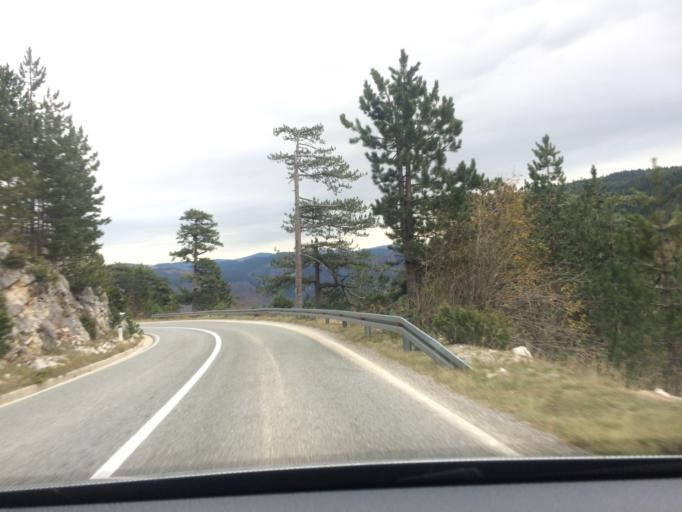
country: ME
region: Opstina Zabljak
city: Zabljak
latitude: 43.1508
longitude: 19.2549
